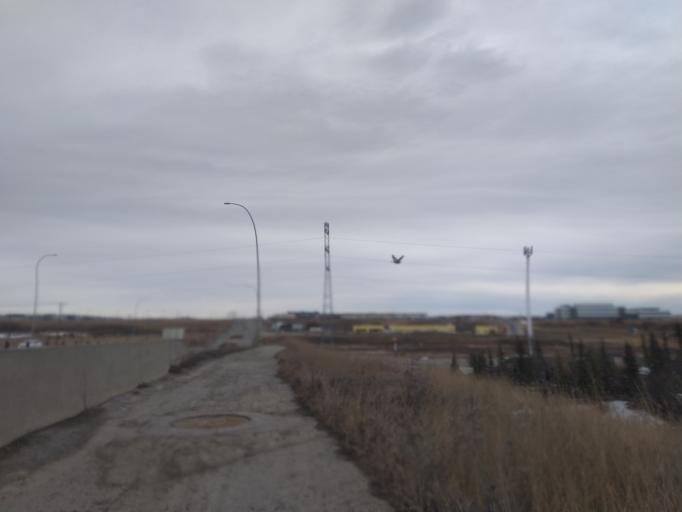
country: CA
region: Alberta
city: Calgary
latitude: 51.1541
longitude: -114.0393
